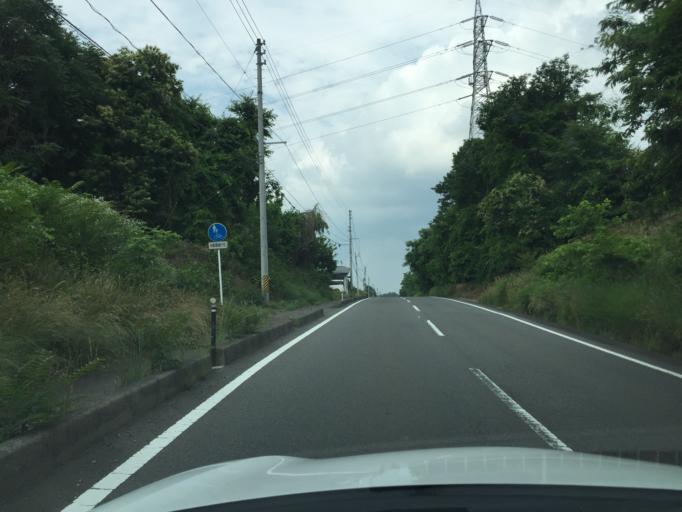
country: JP
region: Fukushima
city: Sukagawa
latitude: 37.2921
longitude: 140.4274
